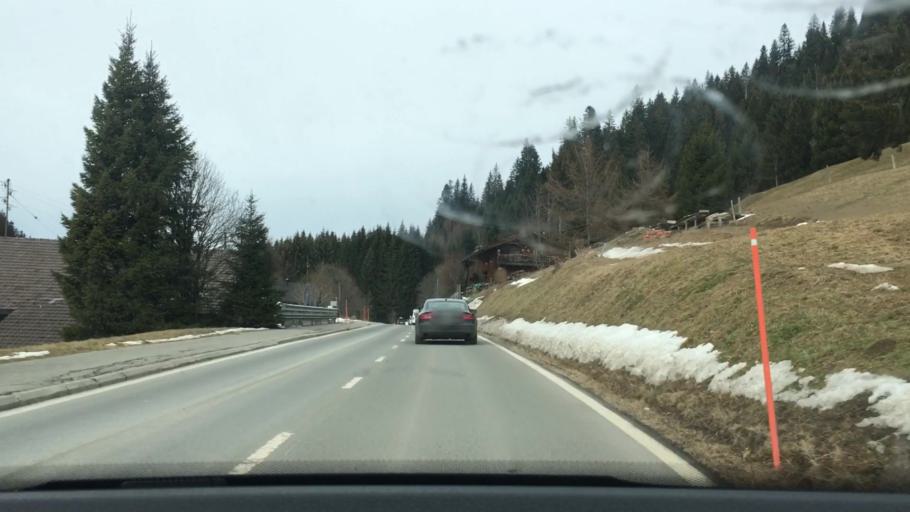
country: FR
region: Rhone-Alpes
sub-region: Departement de la Haute-Savoie
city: Chatel
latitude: 46.2449
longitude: 6.8505
